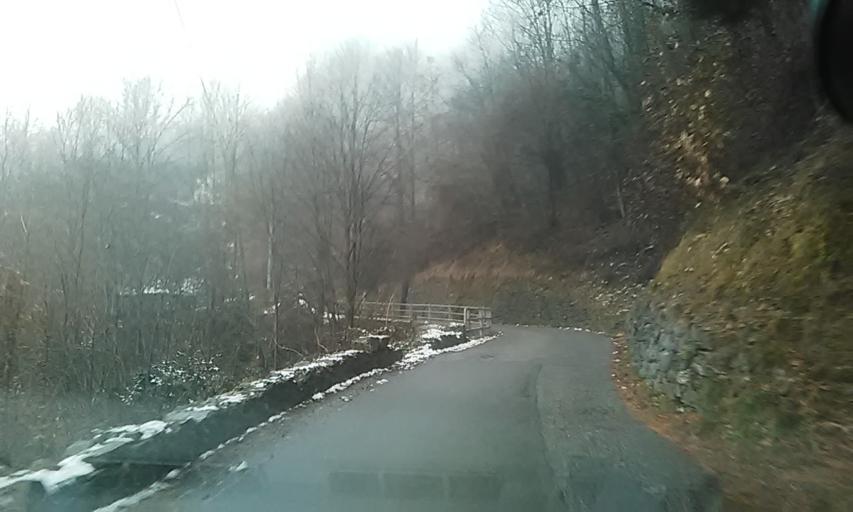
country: IT
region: Piedmont
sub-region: Provincia di Vercelli
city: Varallo
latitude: 45.8389
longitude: 8.2654
